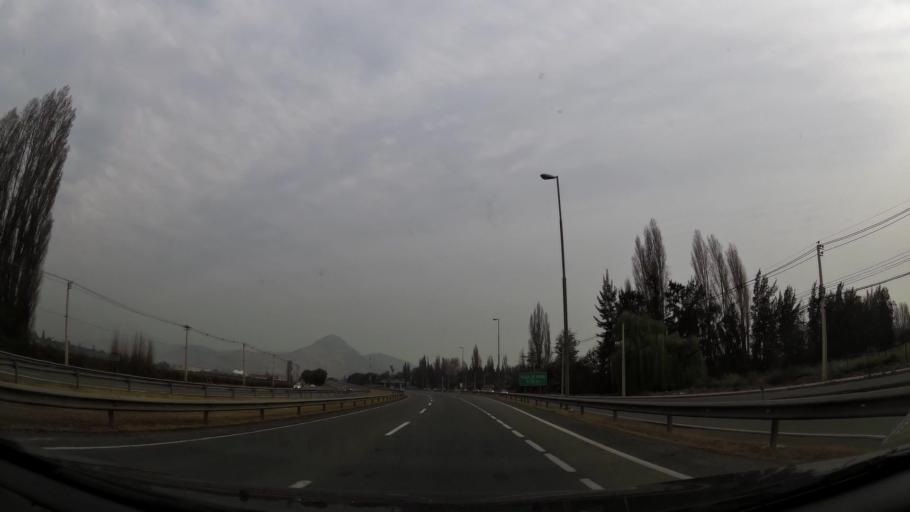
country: CL
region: Santiago Metropolitan
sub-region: Provincia de Chacabuco
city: Chicureo Abajo
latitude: -33.2802
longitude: -70.7031
